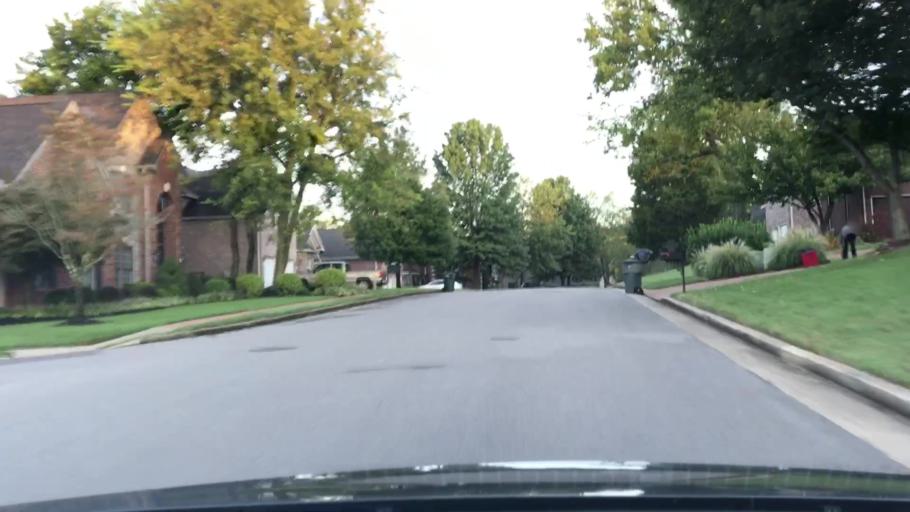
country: US
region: Tennessee
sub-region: Williamson County
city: Brentwood Estates
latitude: 36.0179
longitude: -86.7363
